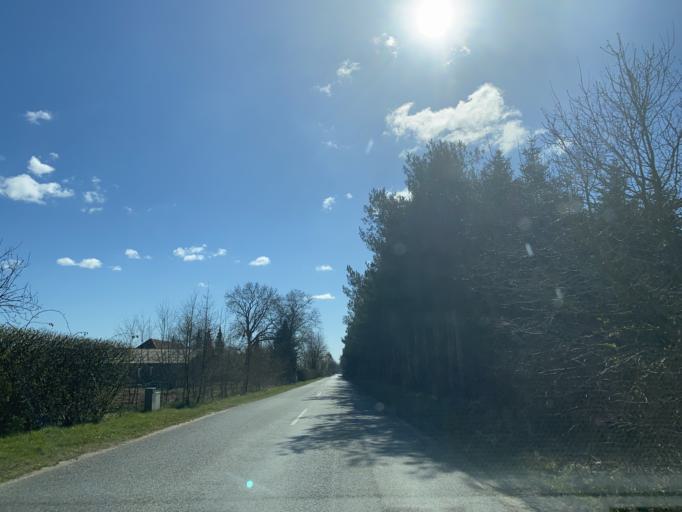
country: DK
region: Central Jutland
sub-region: Silkeborg Kommune
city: Svejbaek
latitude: 56.2428
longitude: 9.6605
